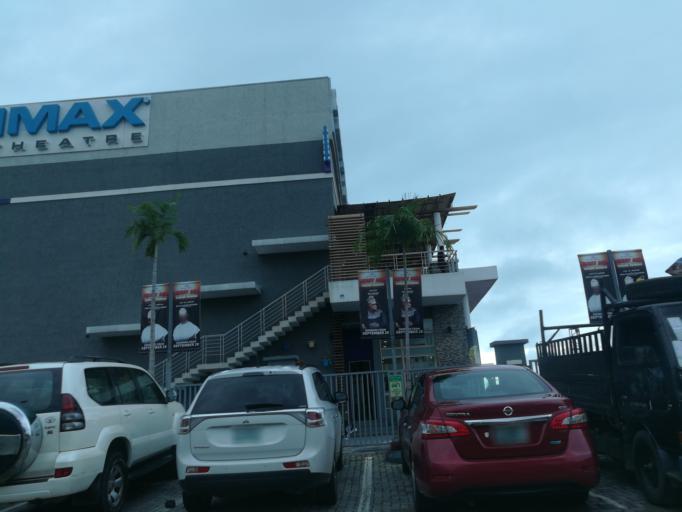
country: NG
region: Lagos
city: Ikoyi
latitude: 6.4397
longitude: 3.4713
